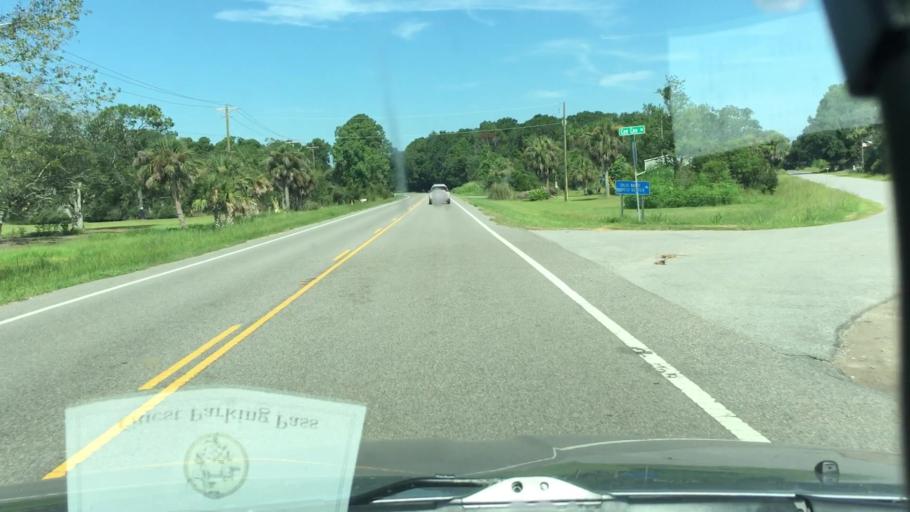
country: US
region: South Carolina
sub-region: Beaufort County
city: Beaufort
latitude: 32.4135
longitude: -80.4792
